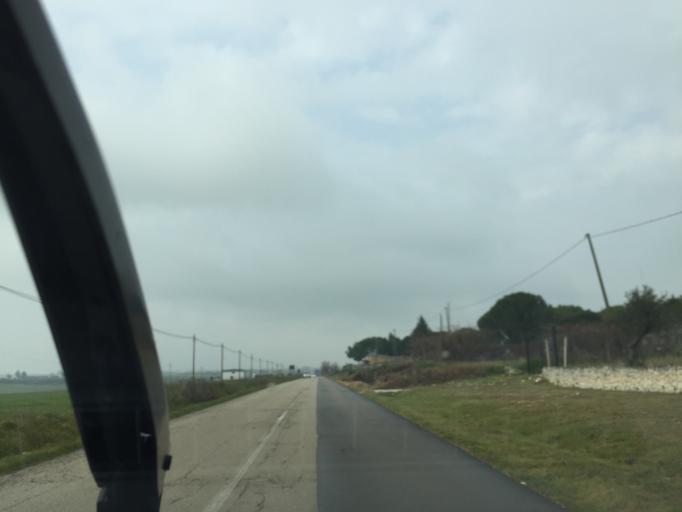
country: IT
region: Apulia
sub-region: Provincia di Foggia
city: Troia
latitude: 41.3808
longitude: 15.3727
